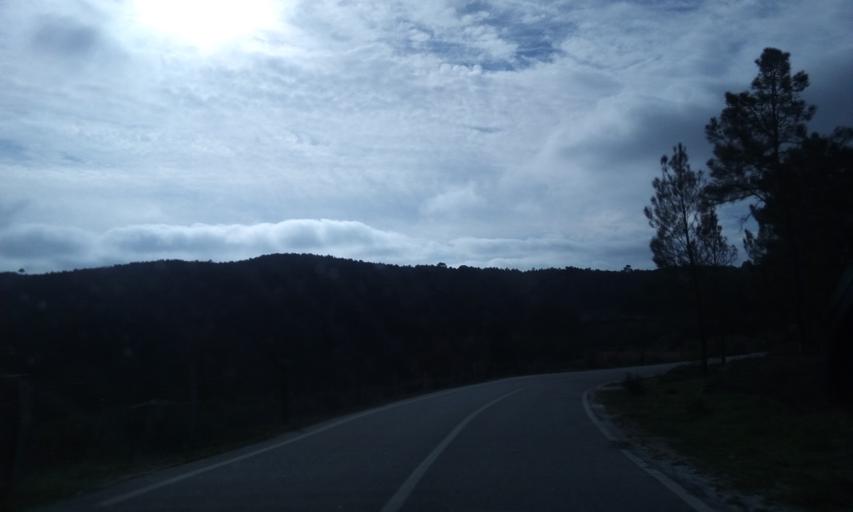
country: PT
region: Guarda
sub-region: Fornos de Algodres
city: Fornos de Algodres
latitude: 40.7223
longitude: -7.5570
